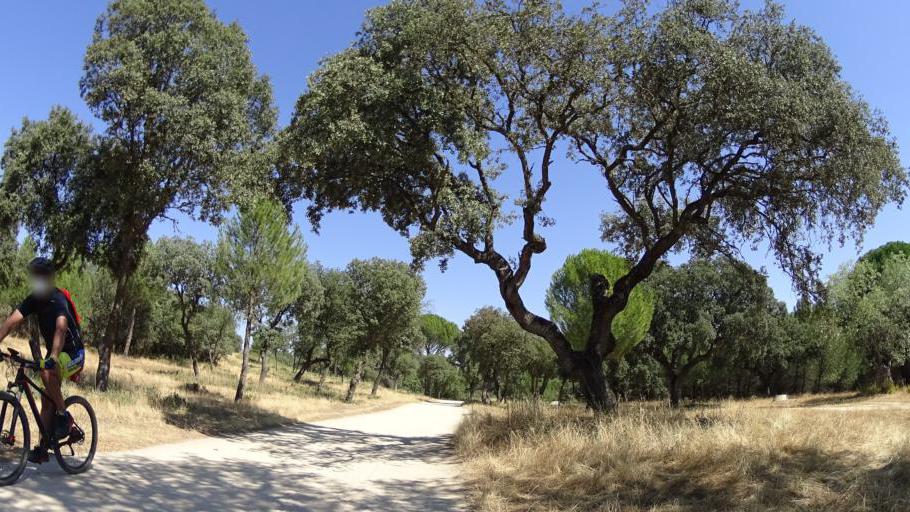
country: ES
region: Madrid
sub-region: Provincia de Madrid
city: Boadilla del Monte
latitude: 40.4241
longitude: -3.8540
